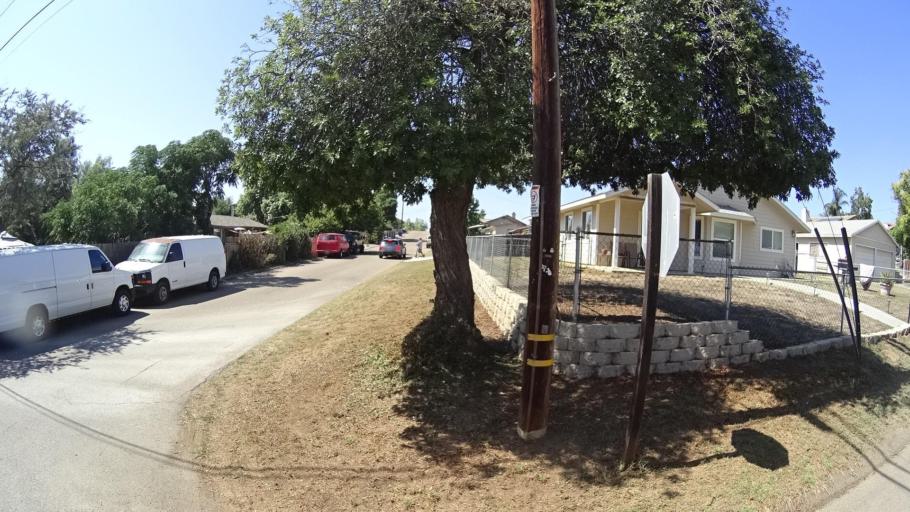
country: US
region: California
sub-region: San Diego County
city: Crest
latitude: 32.8080
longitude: -116.8653
